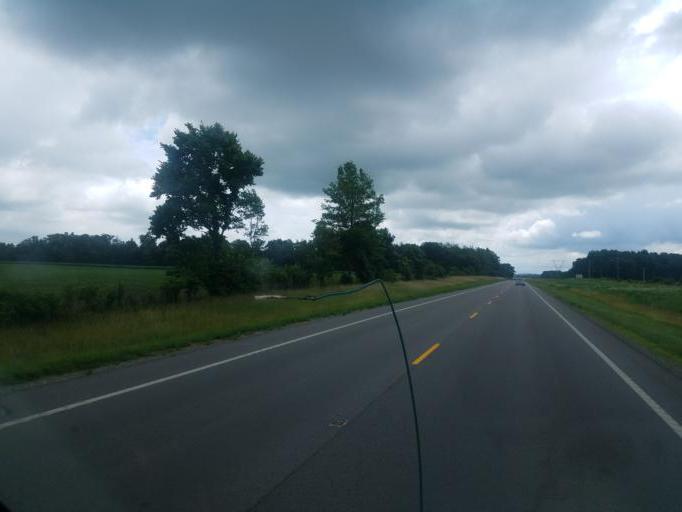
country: US
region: Ohio
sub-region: Logan County
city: Russells Point
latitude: 40.4559
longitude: -83.8488
